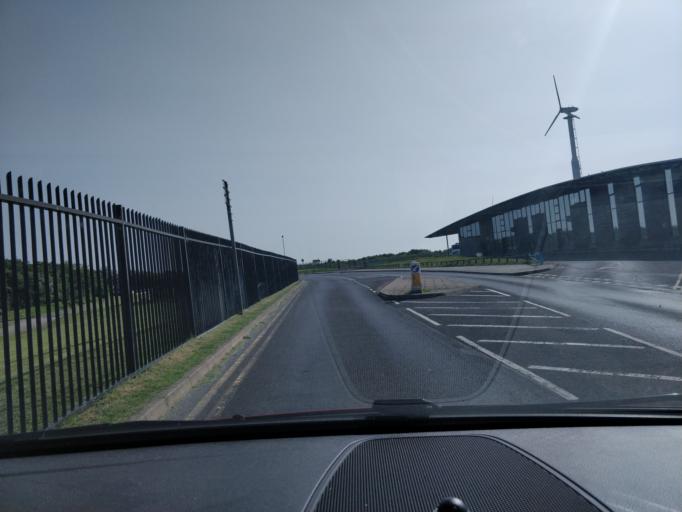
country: GB
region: England
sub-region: Sefton
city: Southport
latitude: 53.6466
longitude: -3.0208
